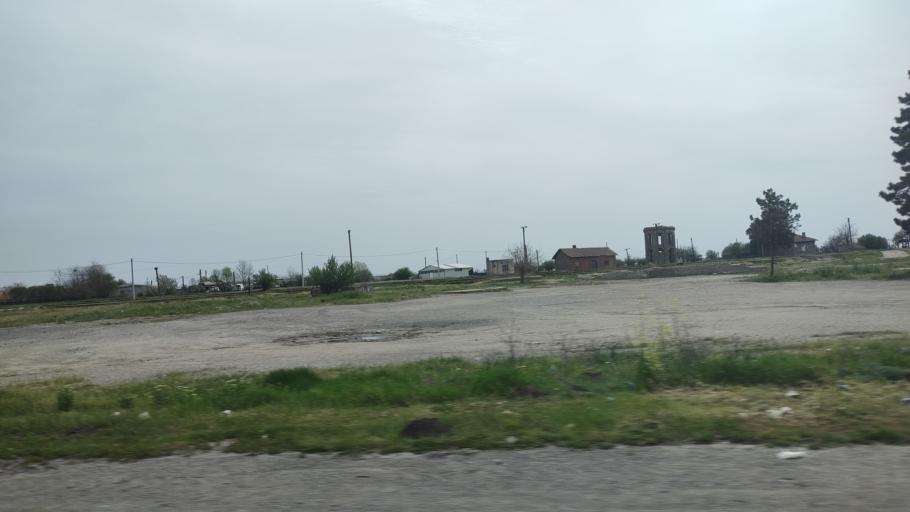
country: RO
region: Constanta
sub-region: Comuna Ciocarlia
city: Ciocarlia
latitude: 44.1017
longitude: 28.2769
